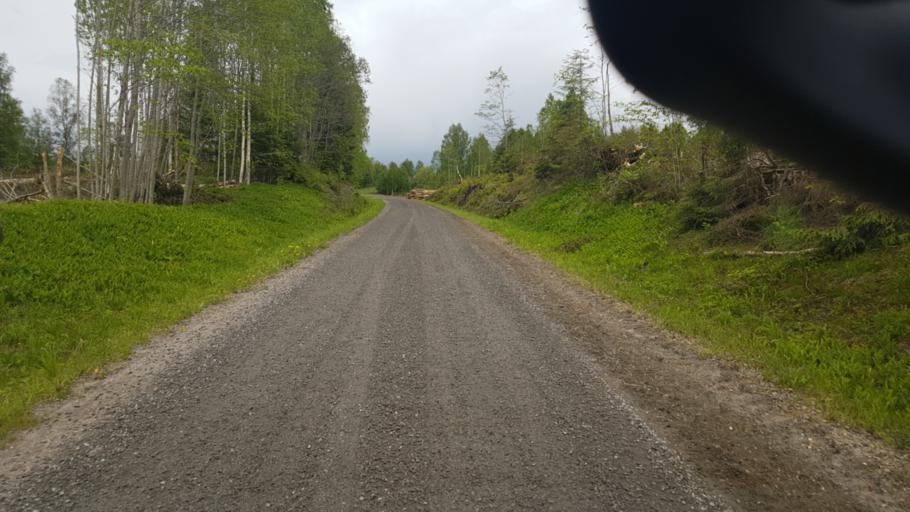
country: SE
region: Vaermland
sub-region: Eda Kommun
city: Charlottenberg
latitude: 59.9926
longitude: 12.5063
